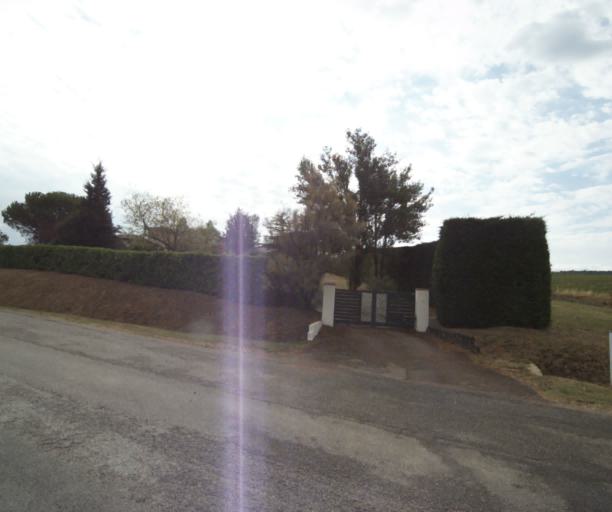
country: FR
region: Midi-Pyrenees
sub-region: Departement de la Haute-Garonne
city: Revel
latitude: 43.4241
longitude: 1.9826
